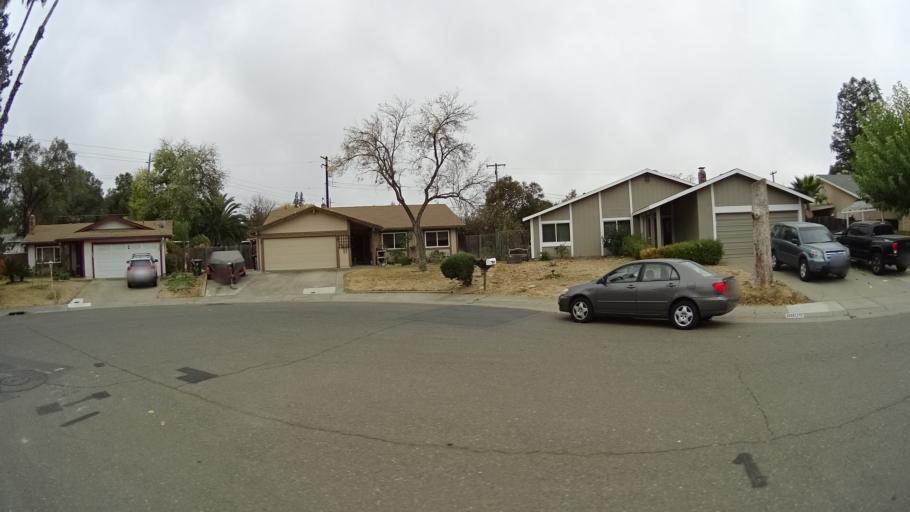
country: US
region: California
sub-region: Sacramento County
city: Citrus Heights
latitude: 38.6907
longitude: -121.3037
